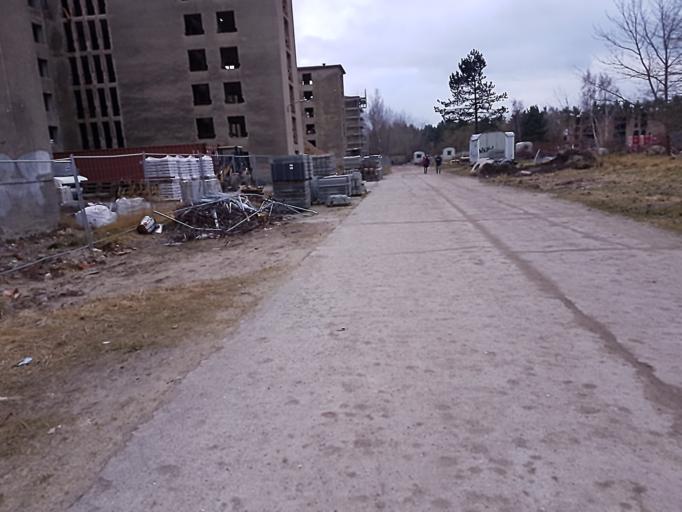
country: DE
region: Mecklenburg-Vorpommern
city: Ostseebad Binz
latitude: 54.4445
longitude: 13.5721
